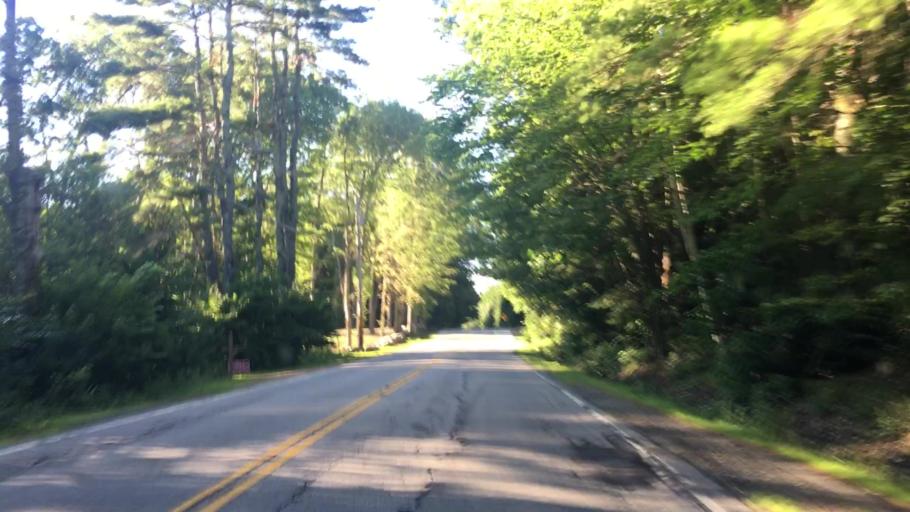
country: US
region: New Hampshire
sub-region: Rockingham County
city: Sandown
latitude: 42.9401
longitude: -71.1934
